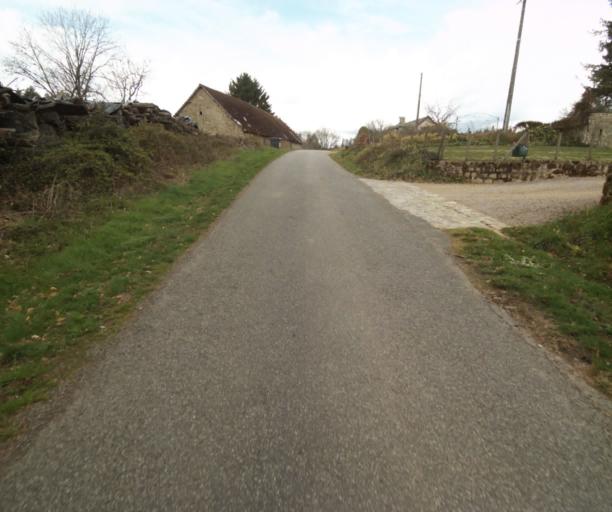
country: FR
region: Limousin
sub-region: Departement de la Correze
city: Correze
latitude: 45.3512
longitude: 1.9333
